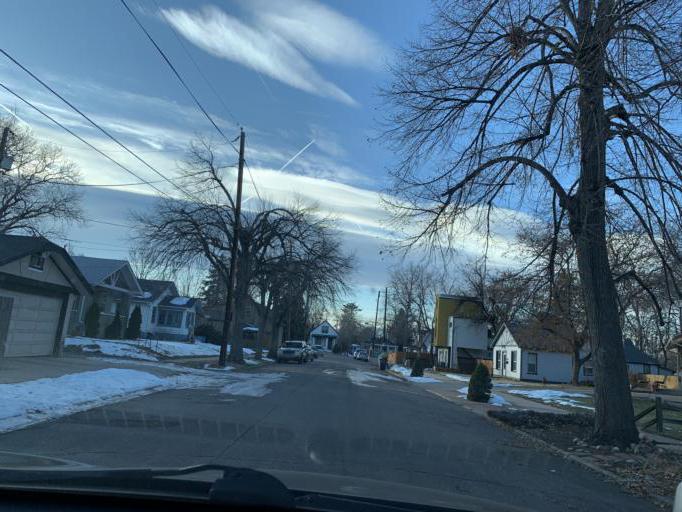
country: US
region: Colorado
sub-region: Adams County
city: Berkley
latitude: 39.7780
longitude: -105.0333
